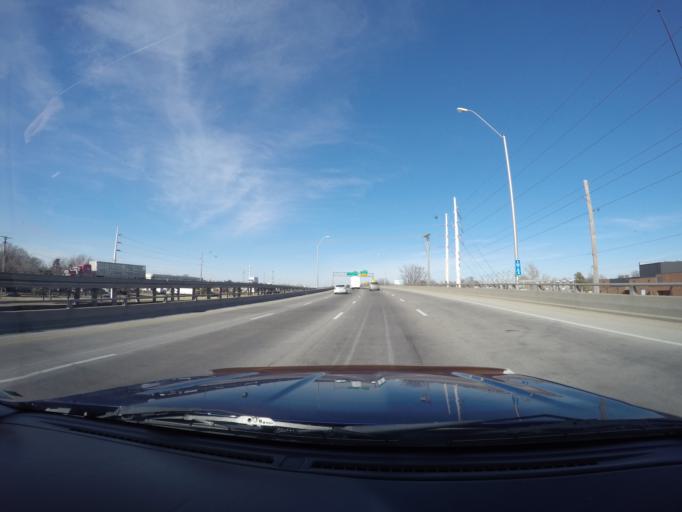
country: US
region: Kansas
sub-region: Sedgwick County
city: Wichita
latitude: 37.6843
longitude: -97.3124
